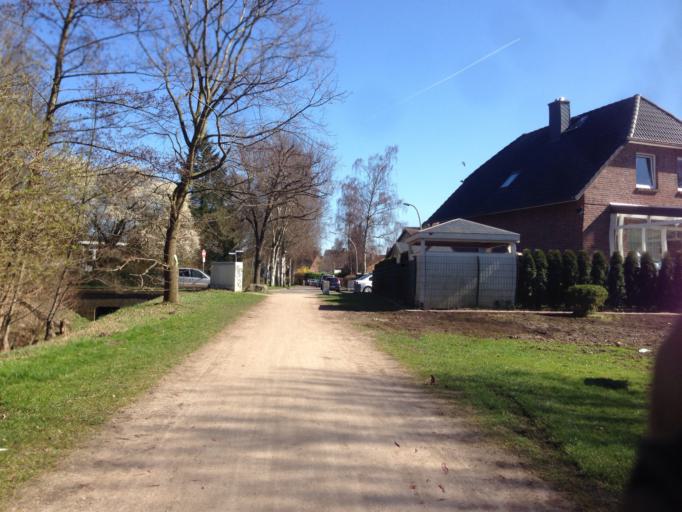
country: DE
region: Hamburg
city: Steilshoop
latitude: 53.5979
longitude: 10.0855
